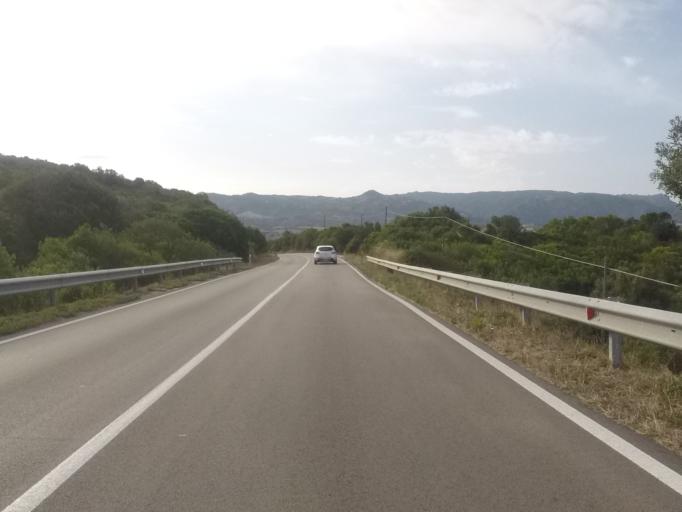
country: IT
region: Sardinia
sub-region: Provincia di Olbia-Tempio
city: Aglientu
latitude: 41.1078
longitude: 9.0624
